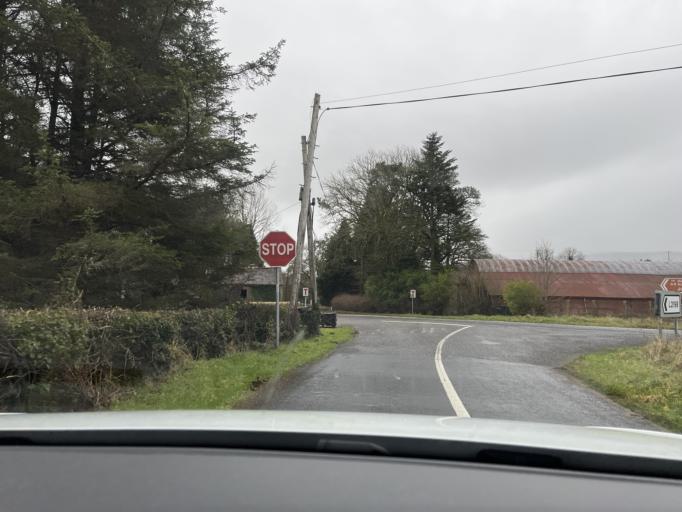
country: IE
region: Connaught
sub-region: County Leitrim
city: Manorhamilton
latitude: 54.2936
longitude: -8.0599
